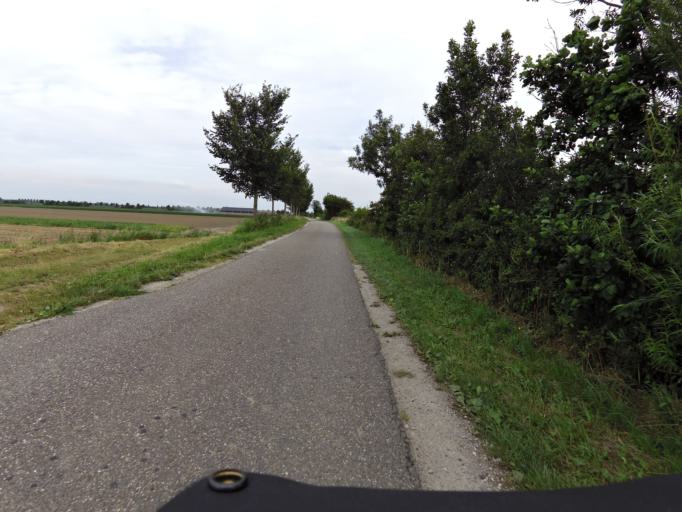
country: NL
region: South Holland
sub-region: Gemeente Goeree-Overflakkee
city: Middelharnis
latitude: 51.7095
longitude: 4.2082
